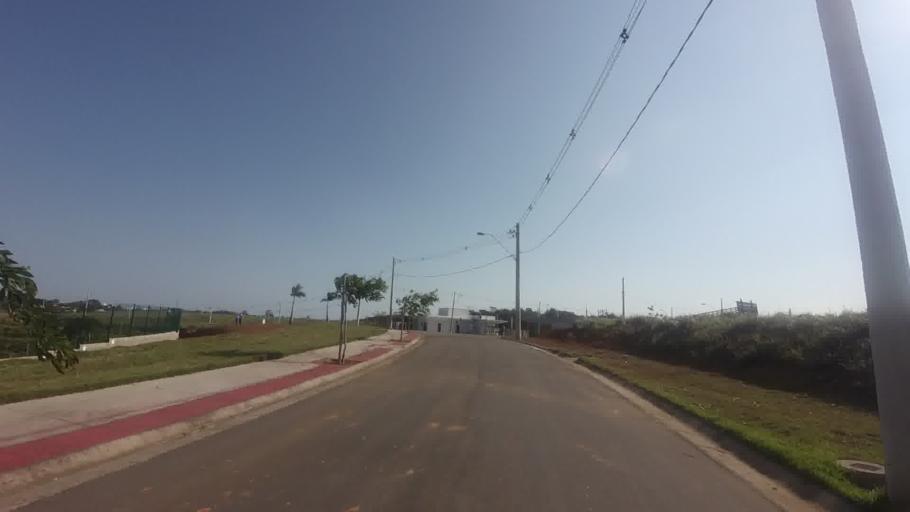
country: BR
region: Espirito Santo
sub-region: Guarapari
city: Guarapari
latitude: -20.7128
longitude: -40.5337
